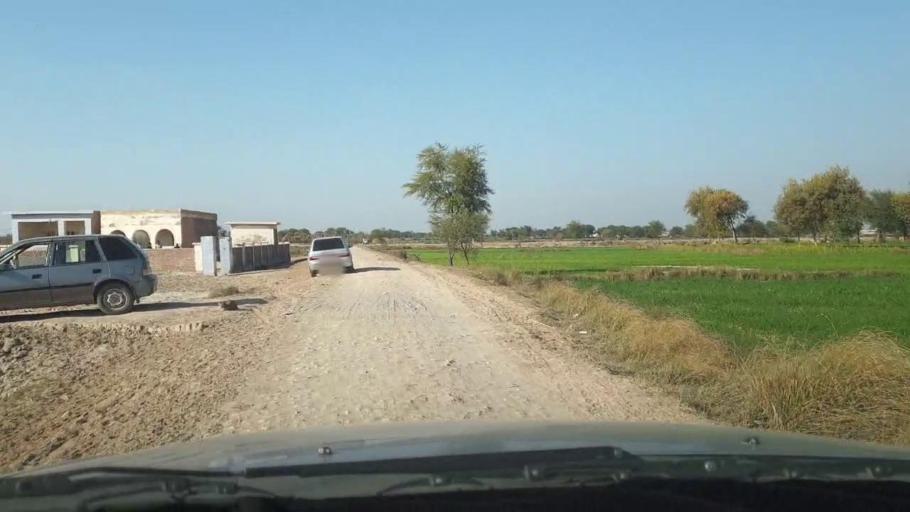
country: PK
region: Sindh
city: Mirpur Mathelo
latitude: 27.9822
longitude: 69.5358
